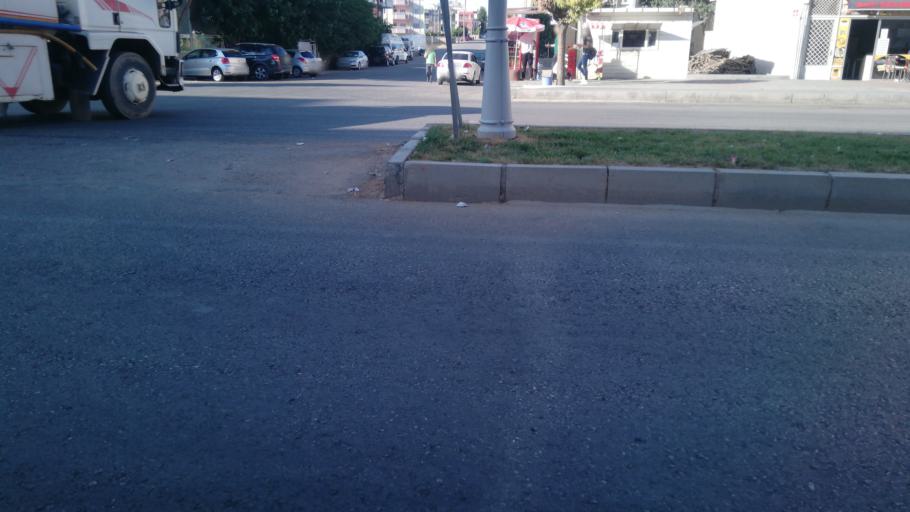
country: TR
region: Mardin
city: Midyat
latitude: 37.4197
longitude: 41.3526
